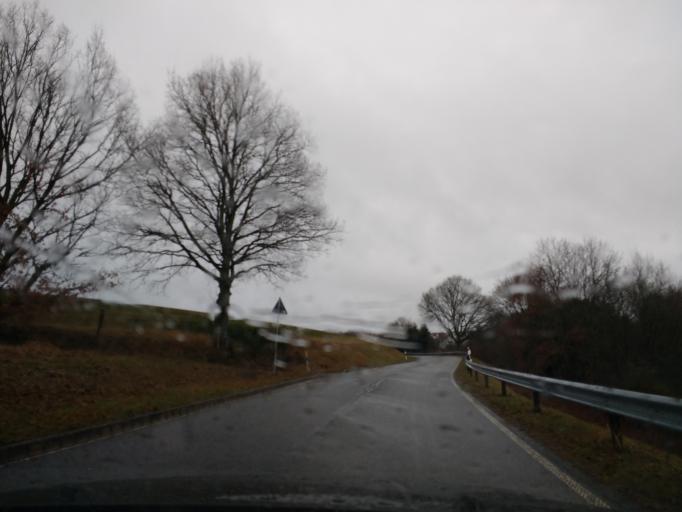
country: DE
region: Rheinland-Pfalz
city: Geisfeld
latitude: 49.7194
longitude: 6.9593
